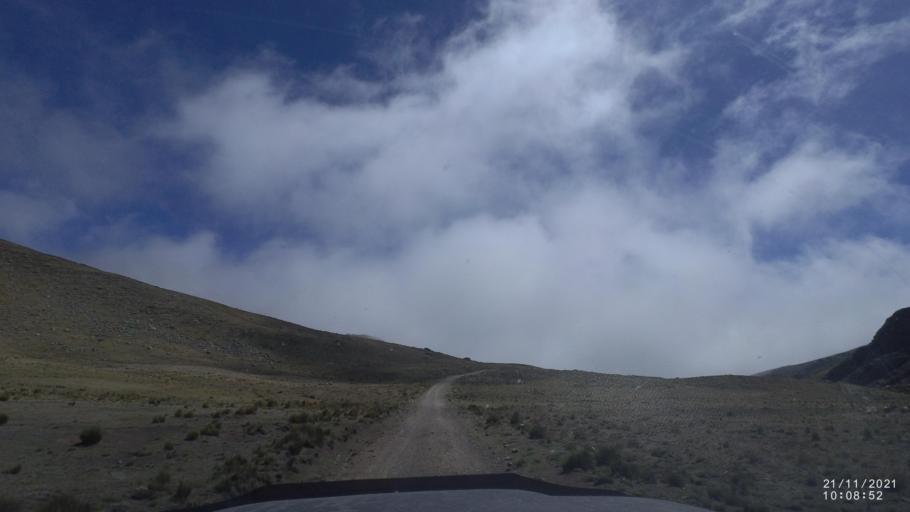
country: BO
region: Cochabamba
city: Cochabamba
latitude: -17.0012
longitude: -66.2804
